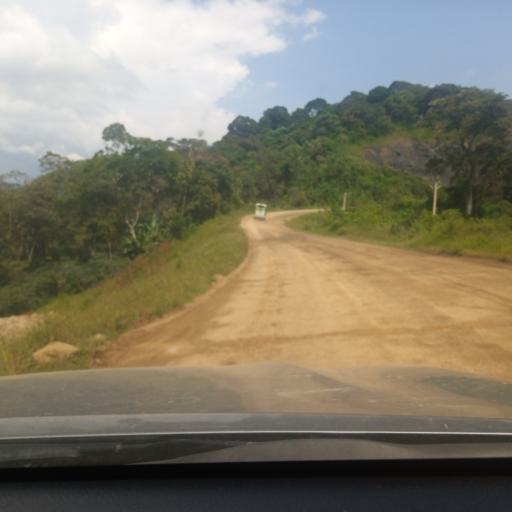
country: ET
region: Southern Nations, Nationalities, and People's Region
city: Tippi
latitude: 7.0697
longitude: 35.4388
